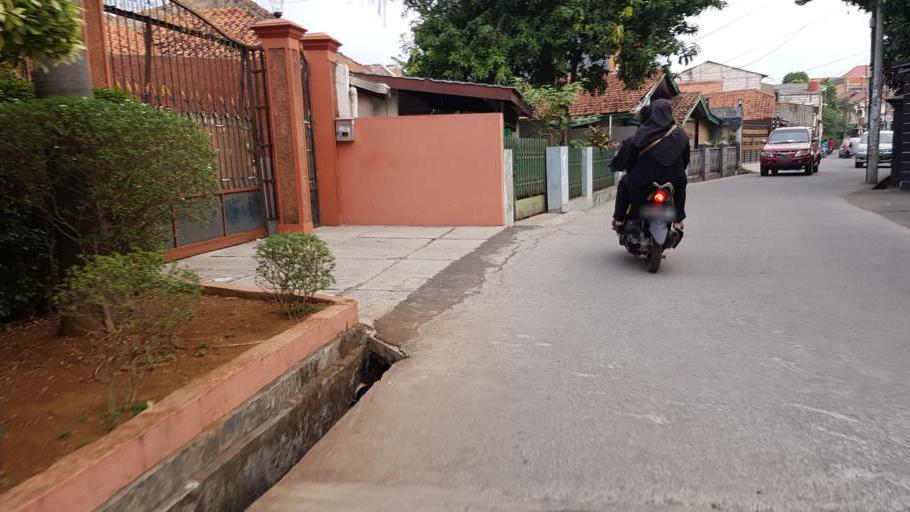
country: ID
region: West Java
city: Bekasi
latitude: -6.2785
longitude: 106.9306
